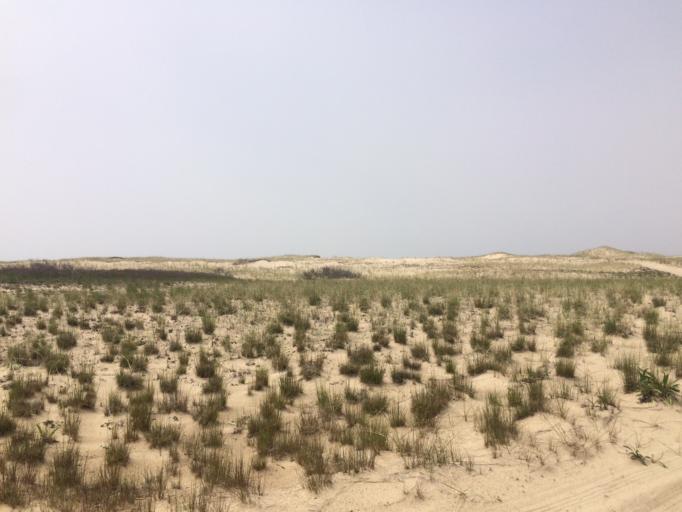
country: US
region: Massachusetts
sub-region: Barnstable County
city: Provincetown
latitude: 42.0644
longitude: -70.2428
